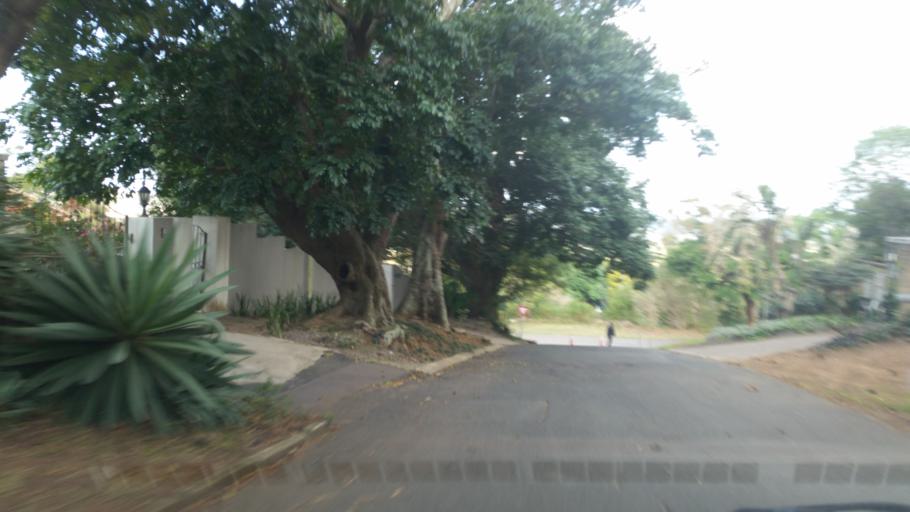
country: ZA
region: KwaZulu-Natal
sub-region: eThekwini Metropolitan Municipality
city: Berea
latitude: -29.8326
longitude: 30.9382
